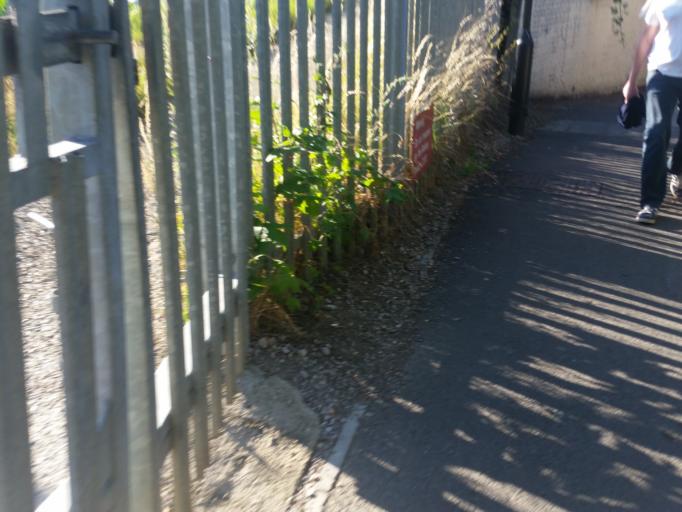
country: GB
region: England
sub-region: Greater London
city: Wood Green
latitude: 51.5927
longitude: -0.1165
